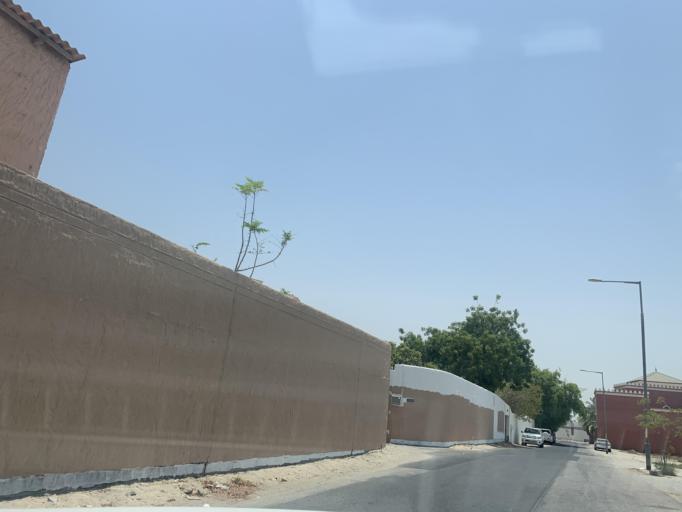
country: BH
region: Manama
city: Jidd Hafs
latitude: 26.2087
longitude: 50.4766
